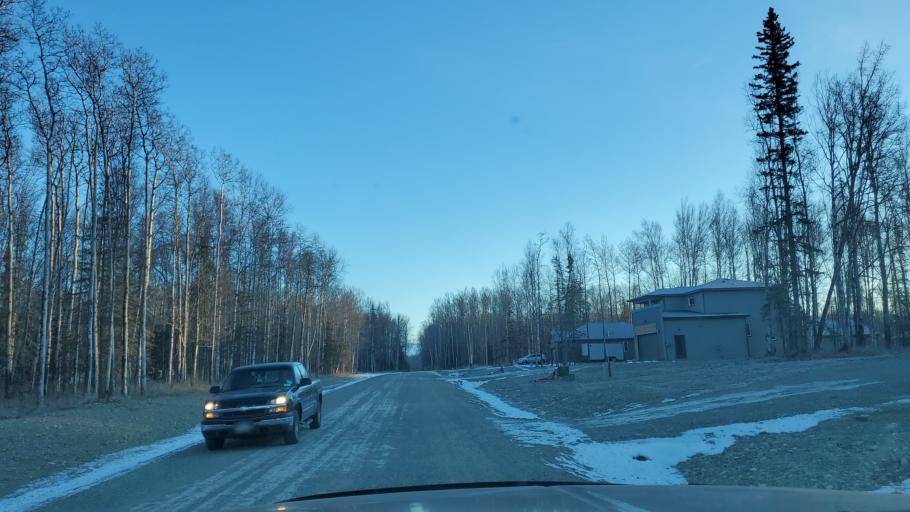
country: US
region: Alaska
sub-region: Matanuska-Susitna Borough
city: Lakes
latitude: 61.6572
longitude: -149.3434
